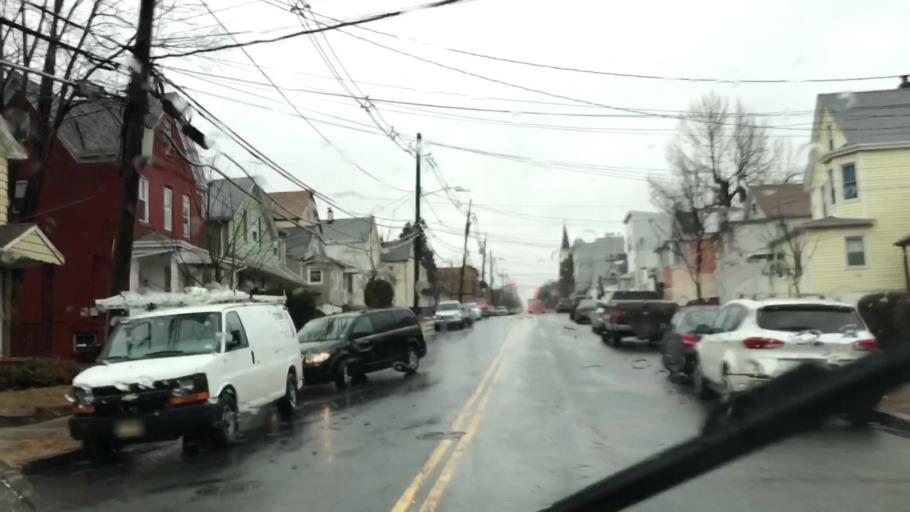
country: US
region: New Jersey
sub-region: Bergen County
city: Garfield
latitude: 40.8736
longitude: -74.1098
